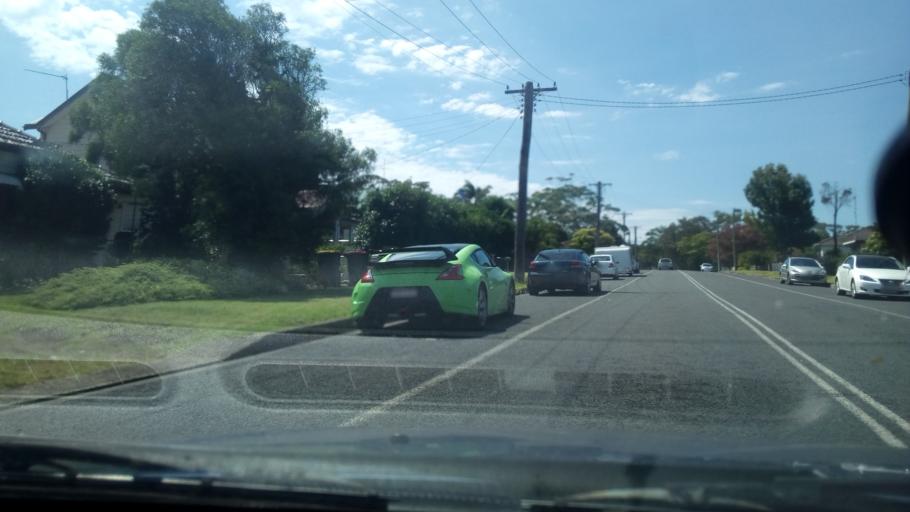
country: AU
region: New South Wales
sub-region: Wollongong
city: Keiraville
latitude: -34.4134
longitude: 150.8752
